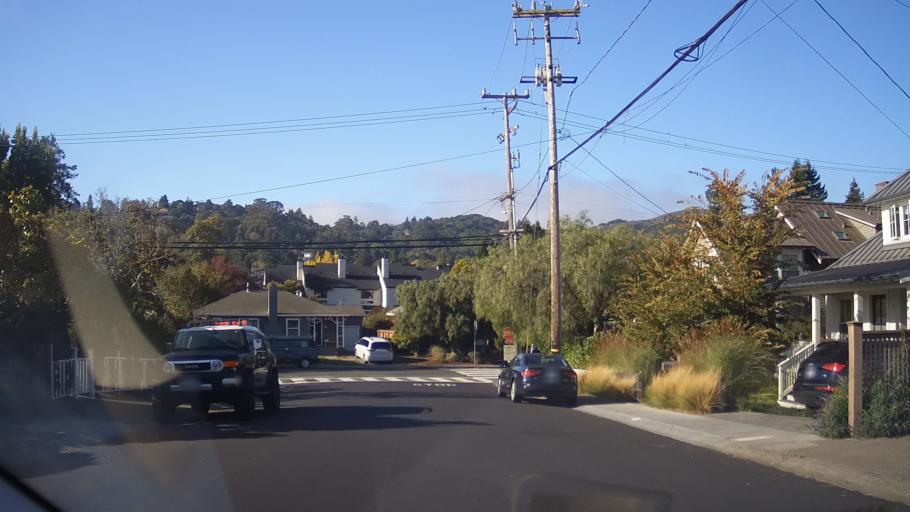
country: US
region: California
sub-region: Marin County
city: Mill Valley
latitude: 37.8981
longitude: -122.5332
